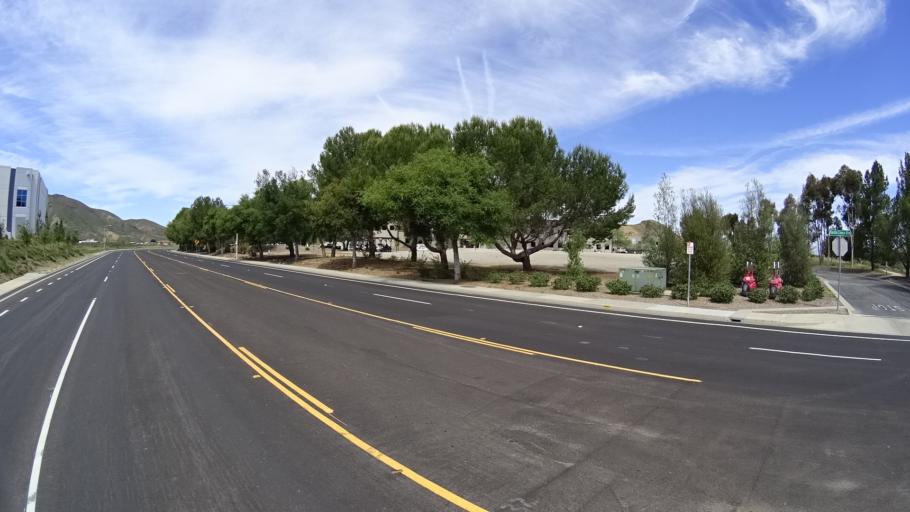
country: US
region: California
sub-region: Ventura County
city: Casa Conejo
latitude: 34.2045
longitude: -118.9281
